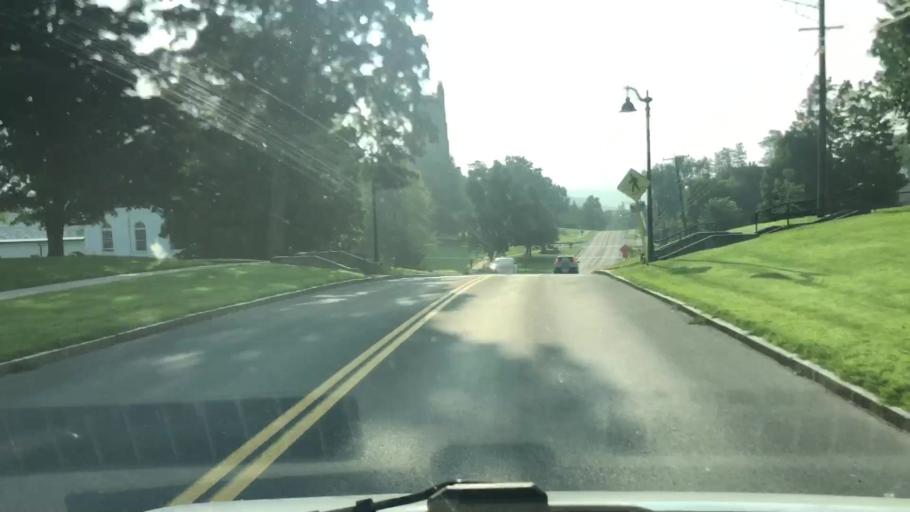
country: US
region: Massachusetts
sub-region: Berkshire County
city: Williamstown
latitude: 42.7127
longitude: -73.2053
